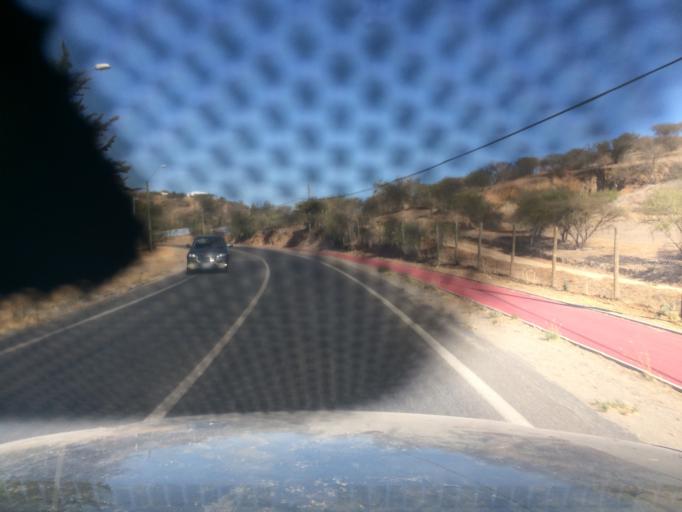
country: CL
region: Santiago Metropolitan
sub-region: Provincia de Melipilla
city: Melipilla
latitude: -33.4941
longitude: -71.1556
